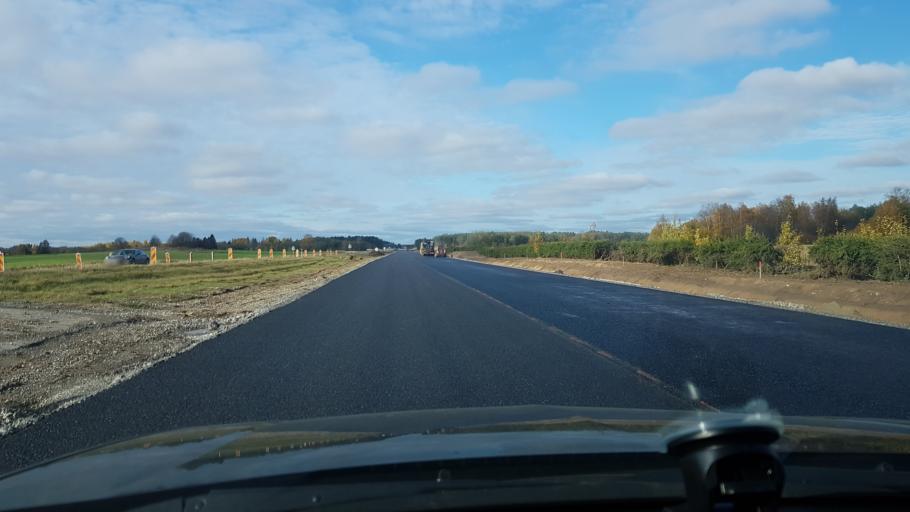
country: EE
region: Laeaene-Virumaa
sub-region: Kadrina vald
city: Kadrina
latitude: 59.4422
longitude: 26.1097
